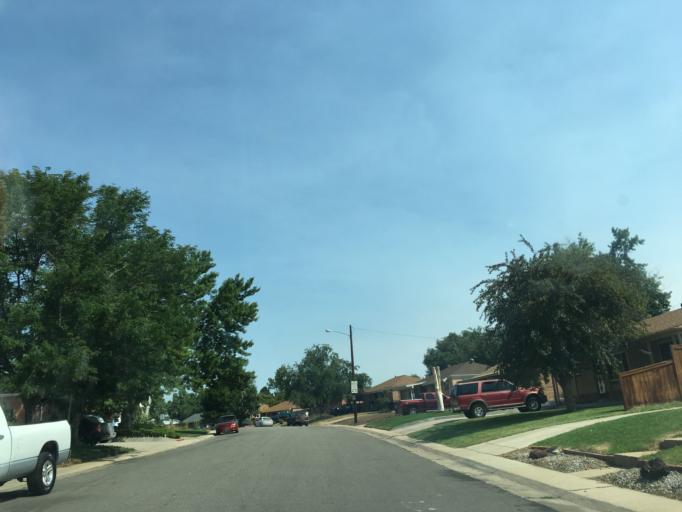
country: US
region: Colorado
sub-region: Jefferson County
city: Lakewood
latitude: 39.6900
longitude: -105.0461
